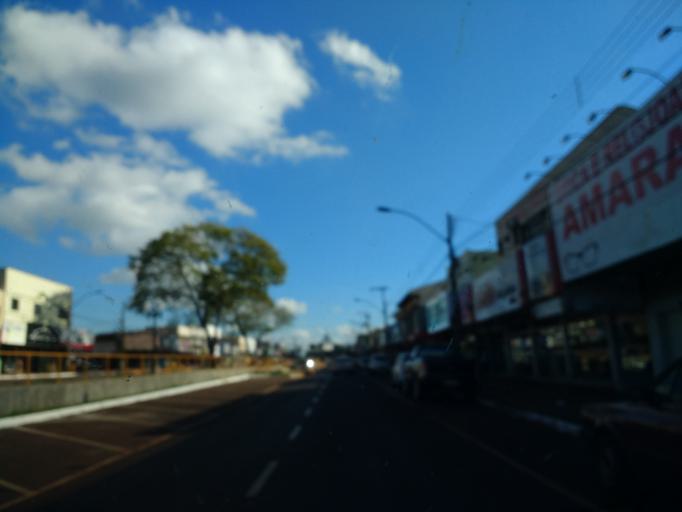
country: BR
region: Parana
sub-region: Palotina
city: Palotina
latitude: -24.4089
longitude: -53.5180
